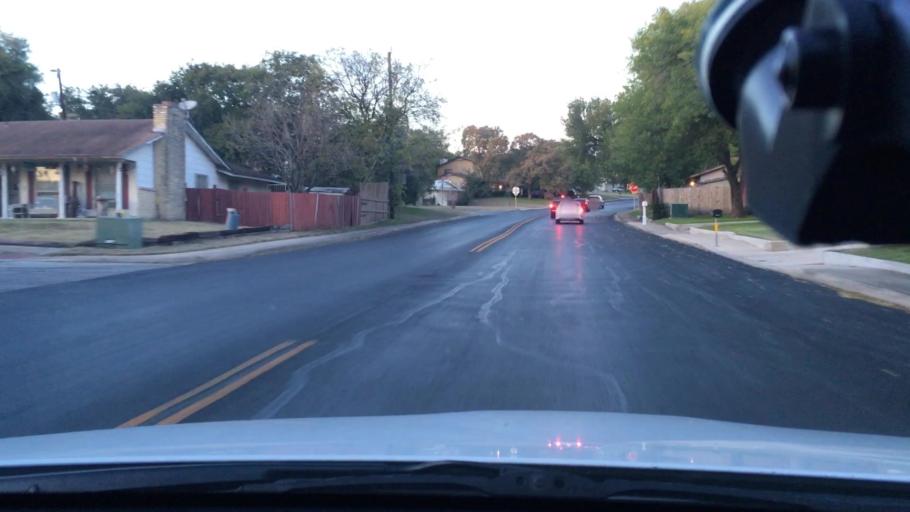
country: US
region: Texas
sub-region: Bexar County
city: Windcrest
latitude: 29.5156
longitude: -98.3565
